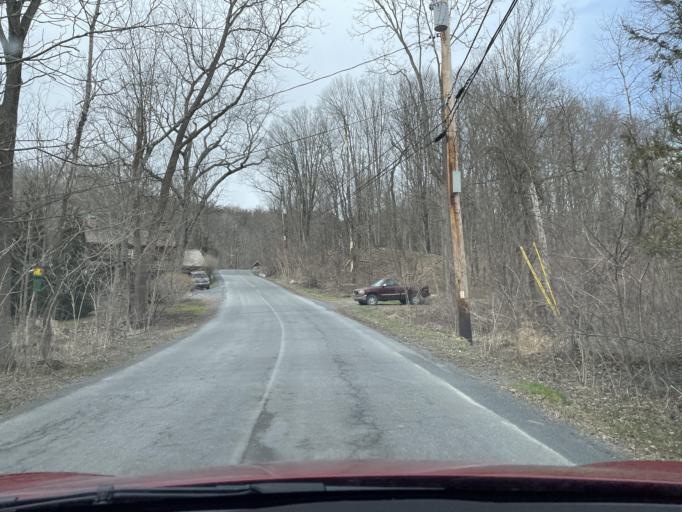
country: US
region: New York
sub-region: Ulster County
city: Saugerties
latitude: 42.1033
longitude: -73.9790
